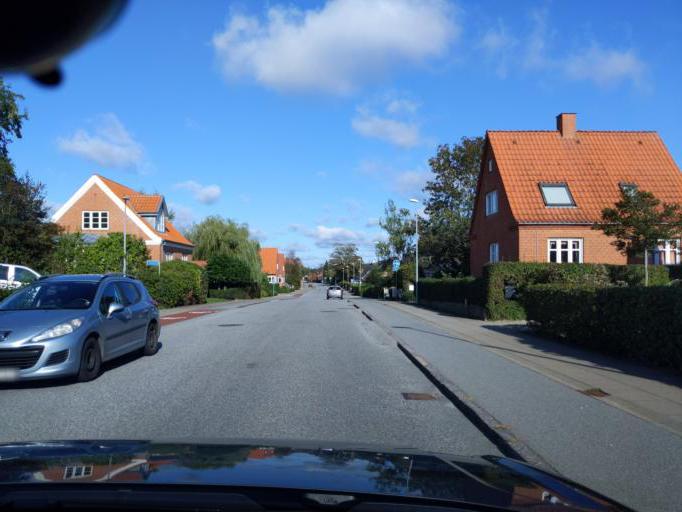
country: DK
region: Central Jutland
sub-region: Viborg Kommune
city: Viborg
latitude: 56.4637
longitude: 9.4213
